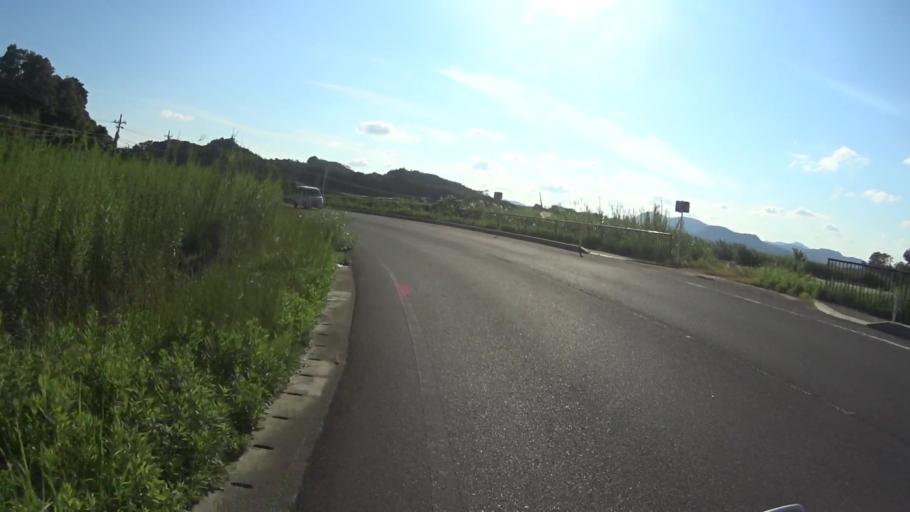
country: JP
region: Hyogo
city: Toyooka
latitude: 35.6445
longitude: 134.9455
